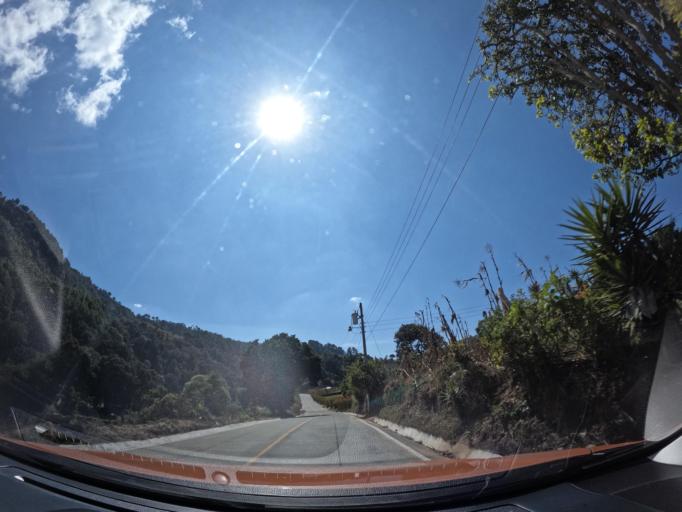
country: GT
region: Solola
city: San Antonio Palopo
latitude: 14.6970
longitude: -91.0698
